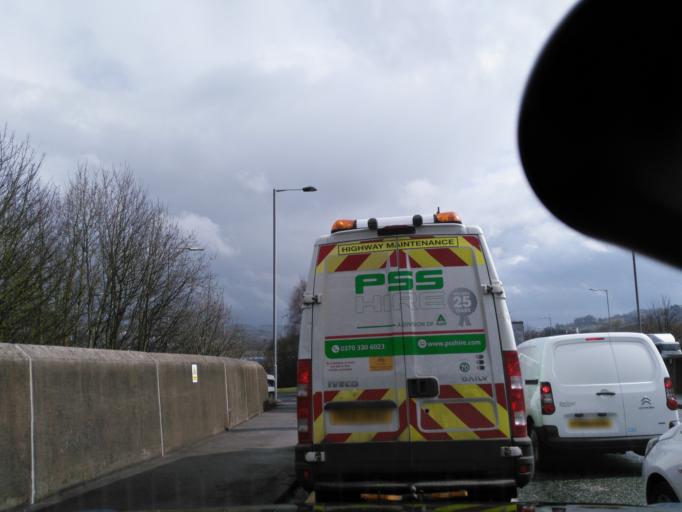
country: GB
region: England
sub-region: Bradford
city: Keighley
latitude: 53.8759
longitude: -1.9079
